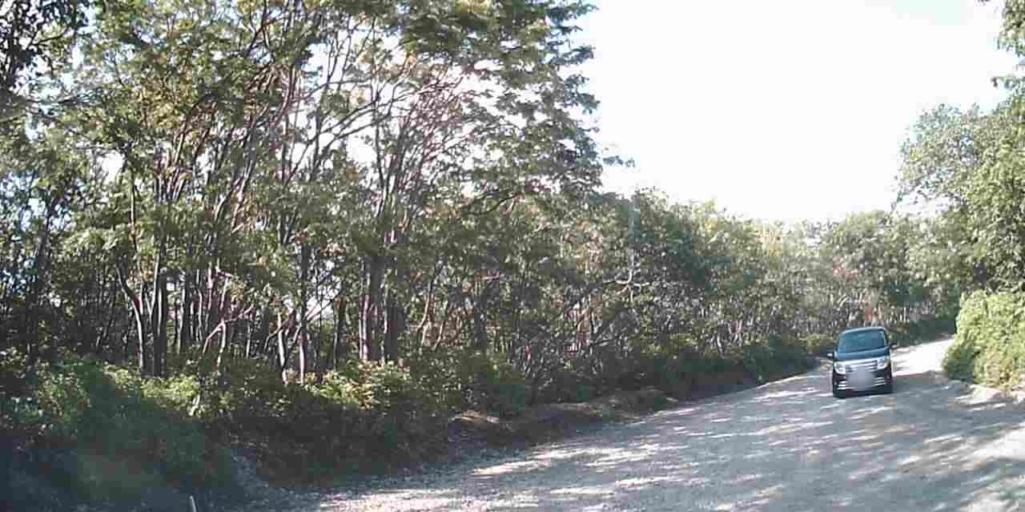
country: JP
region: Hokkaido
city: Shiraoi
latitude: 42.6997
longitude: 141.3898
